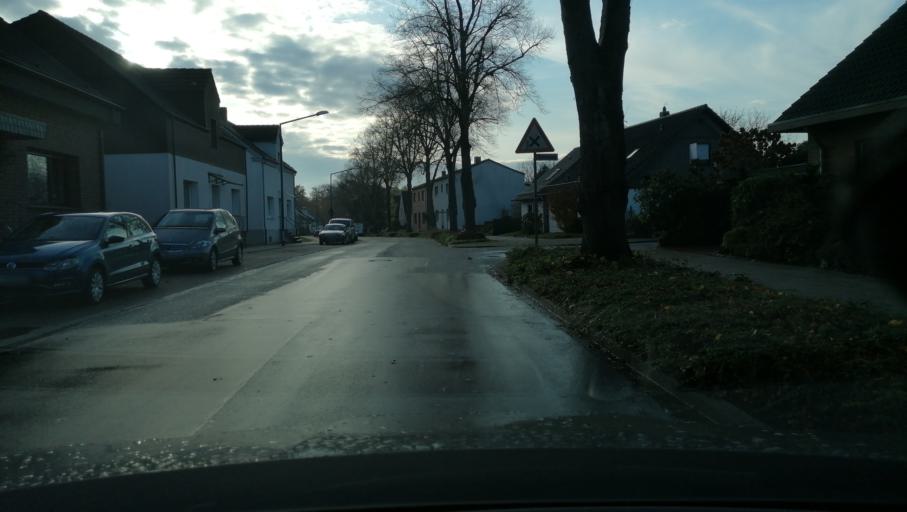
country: DE
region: North Rhine-Westphalia
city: Herten
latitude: 51.5947
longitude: 7.1509
